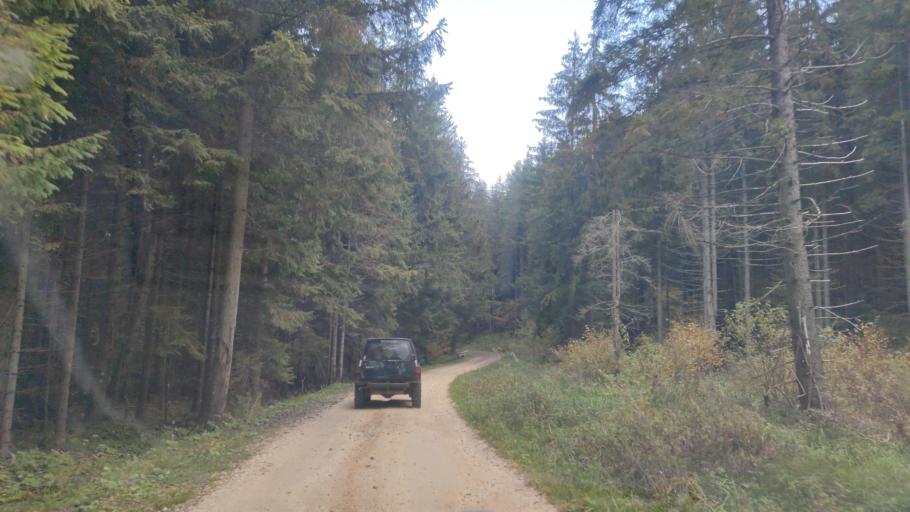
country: RO
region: Harghita
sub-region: Comuna Madaras
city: Madaras
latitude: 46.4855
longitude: 25.6701
